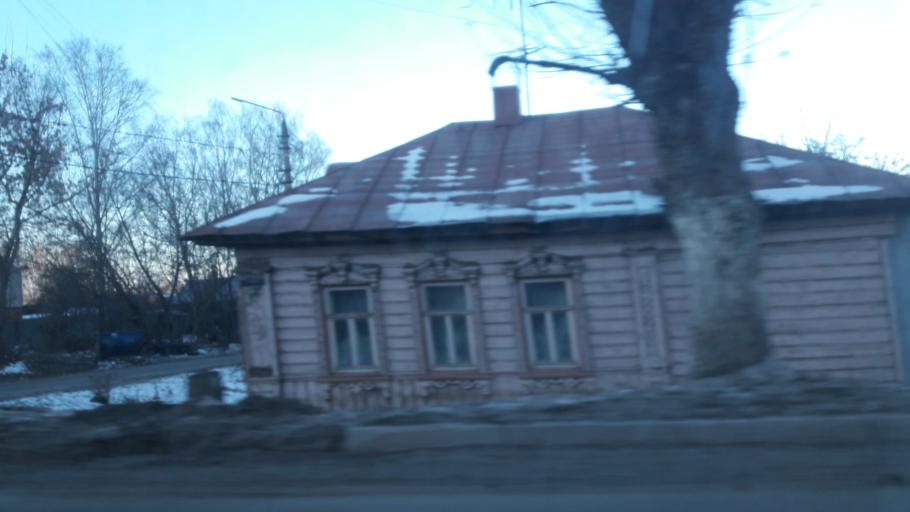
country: RU
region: Tula
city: Tula
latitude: 54.2021
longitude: 37.6379
